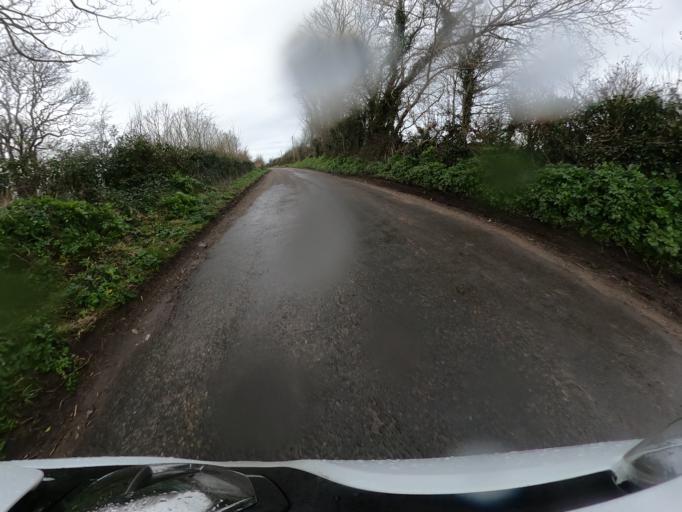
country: IM
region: Ramsey
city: Ramsey
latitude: 54.3779
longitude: -4.4540
